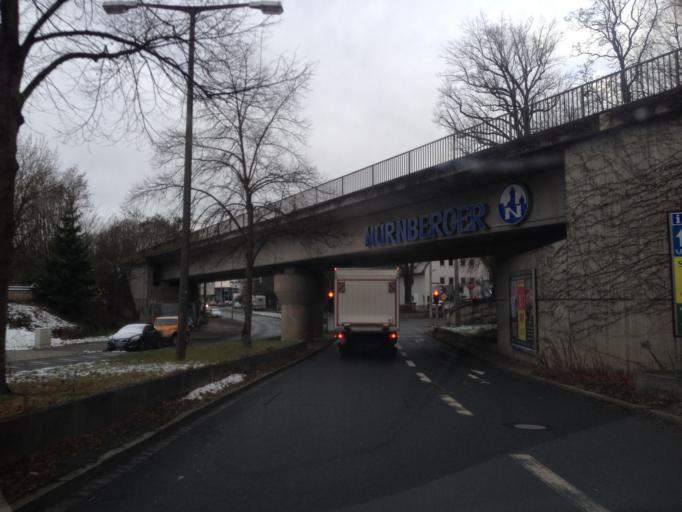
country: DE
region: Bavaria
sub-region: Regierungsbezirk Mittelfranken
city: Schwaig
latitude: 49.4723
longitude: 11.1395
